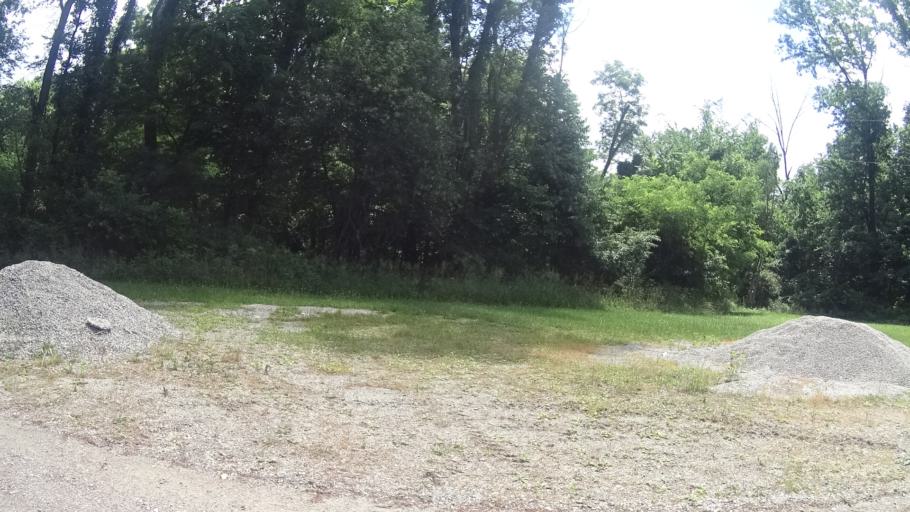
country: US
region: Ohio
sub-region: Lorain County
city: Camden
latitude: 41.2949
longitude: -82.3431
